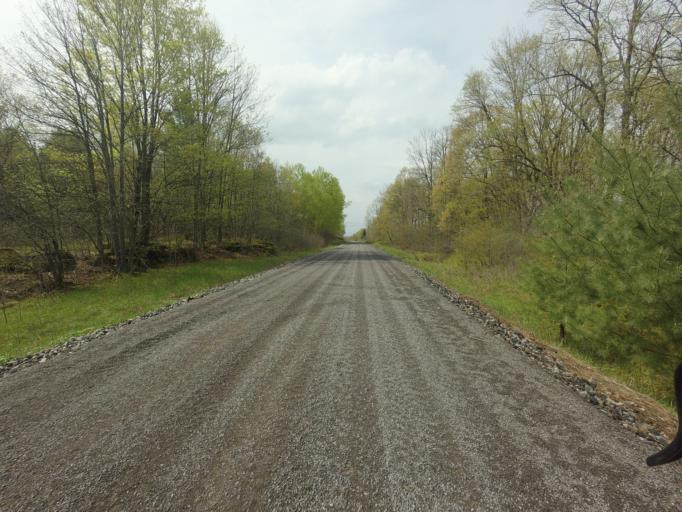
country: CA
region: Ontario
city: Carleton Place
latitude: 45.1610
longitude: -76.1461
